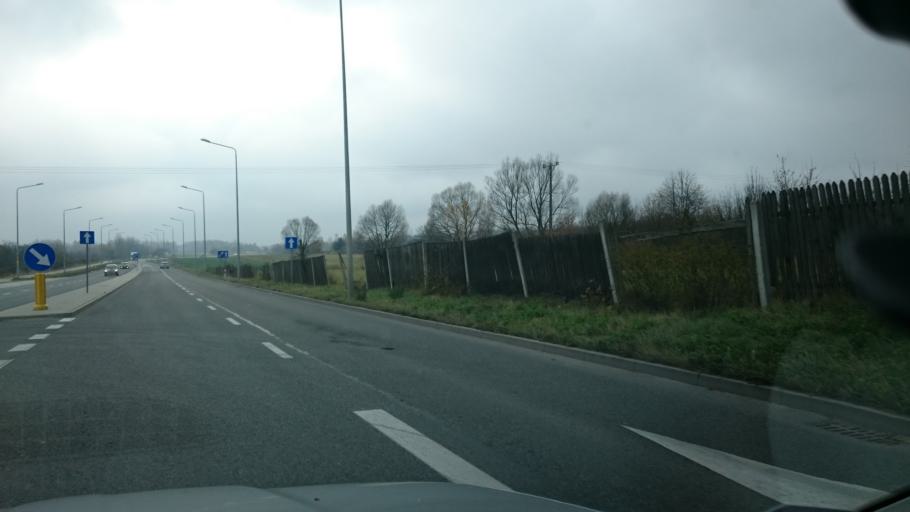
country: PL
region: Swietokrzyskie
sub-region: Powiat konecki
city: Konskie
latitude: 51.1867
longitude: 20.3966
